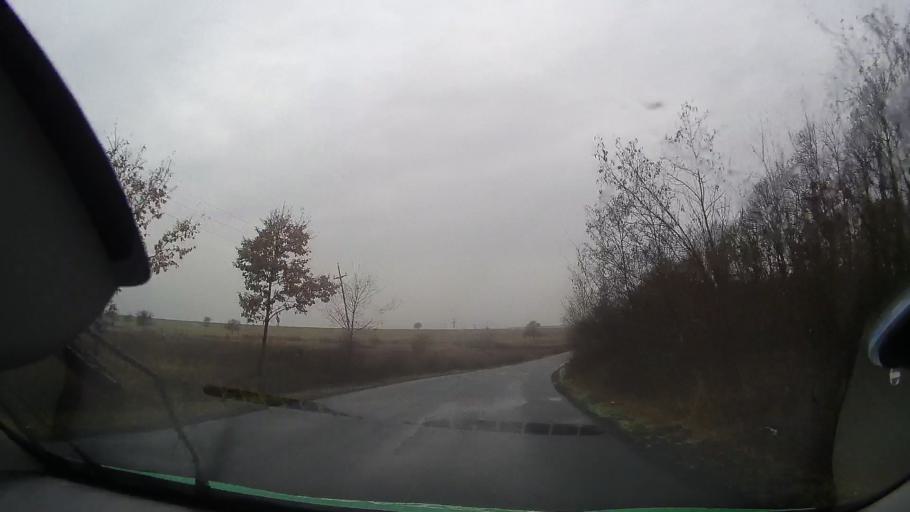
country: RO
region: Bihor
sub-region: Comuna Tinca
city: Gurbediu
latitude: 46.7748
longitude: 21.8830
